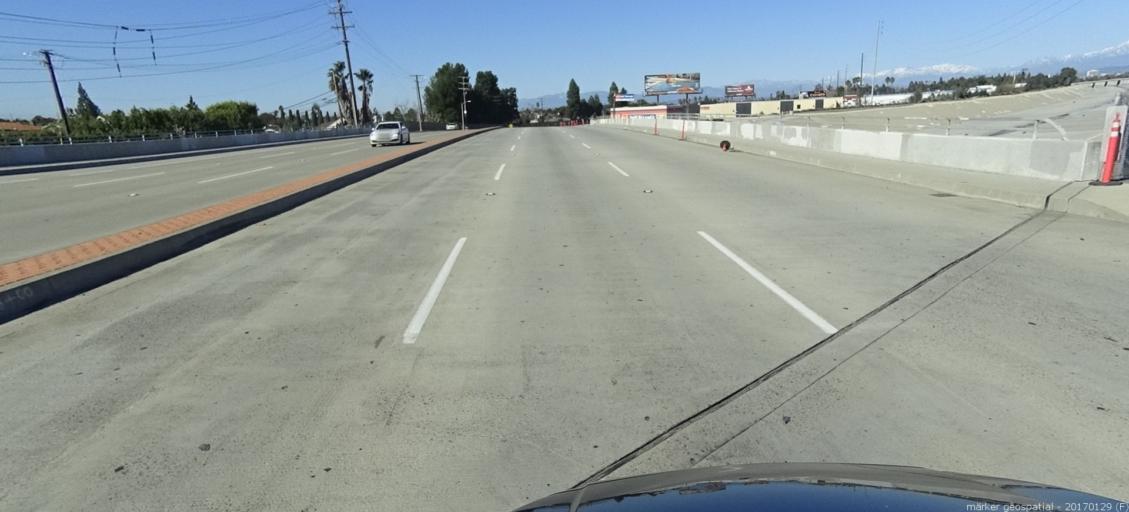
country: US
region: California
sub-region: Orange County
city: Fountain Valley
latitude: 33.7159
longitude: -117.9202
